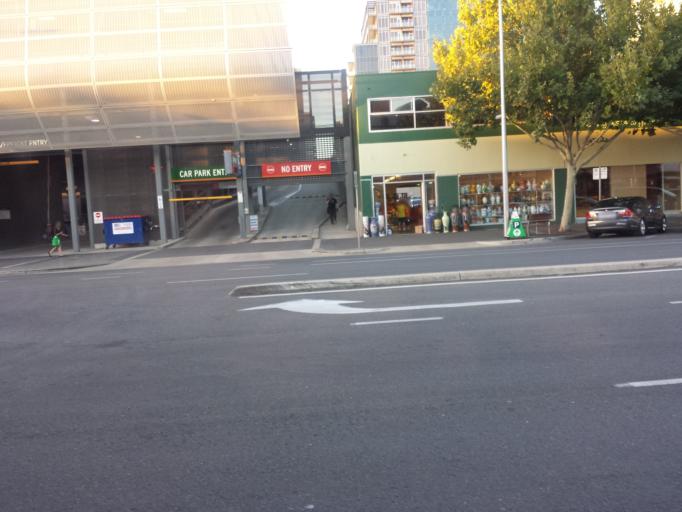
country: AU
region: South Australia
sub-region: Adelaide
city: Adelaide
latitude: -34.9289
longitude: 138.5962
